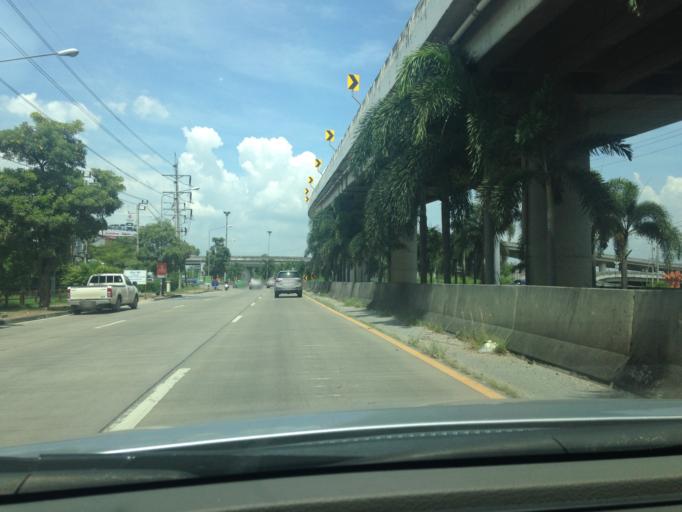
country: TH
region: Bangkok
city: Lat Krabang
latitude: 13.7155
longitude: 100.7401
